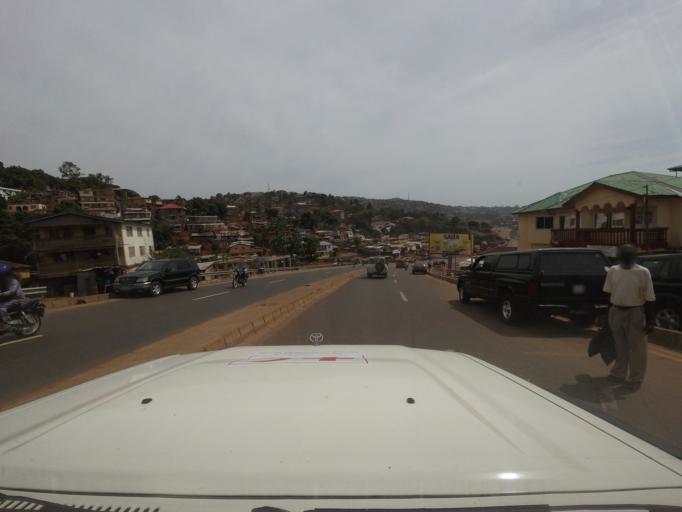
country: SL
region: Western Area
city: Freetown
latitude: 8.4762
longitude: -13.2310
